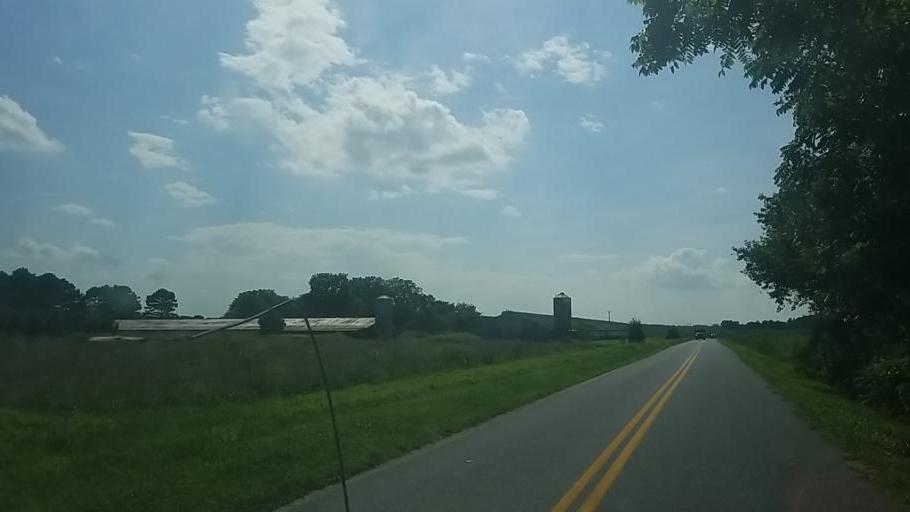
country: US
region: Maryland
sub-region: Somerset County
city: Princess Anne
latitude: 38.2614
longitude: -75.6789
